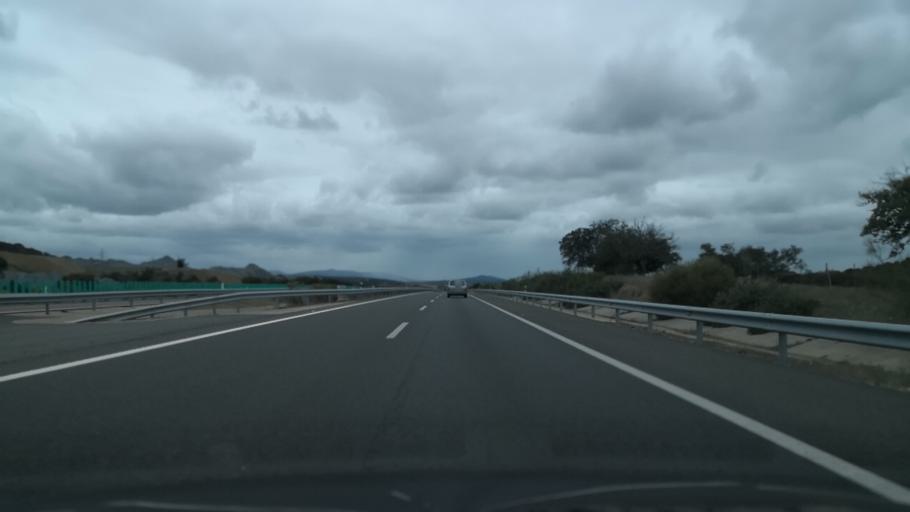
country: ES
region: Extremadura
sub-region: Provincia de Caceres
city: Galisteo
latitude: 39.9572
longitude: -6.1770
